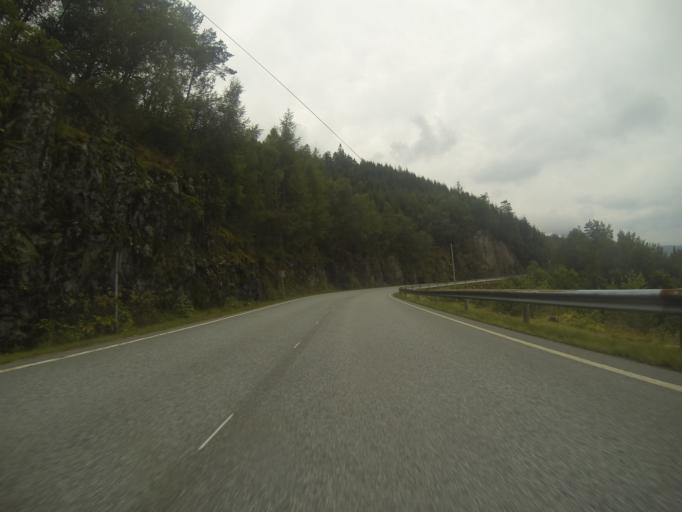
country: NO
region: Rogaland
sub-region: Suldal
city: Sand
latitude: 59.5517
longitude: 6.2604
